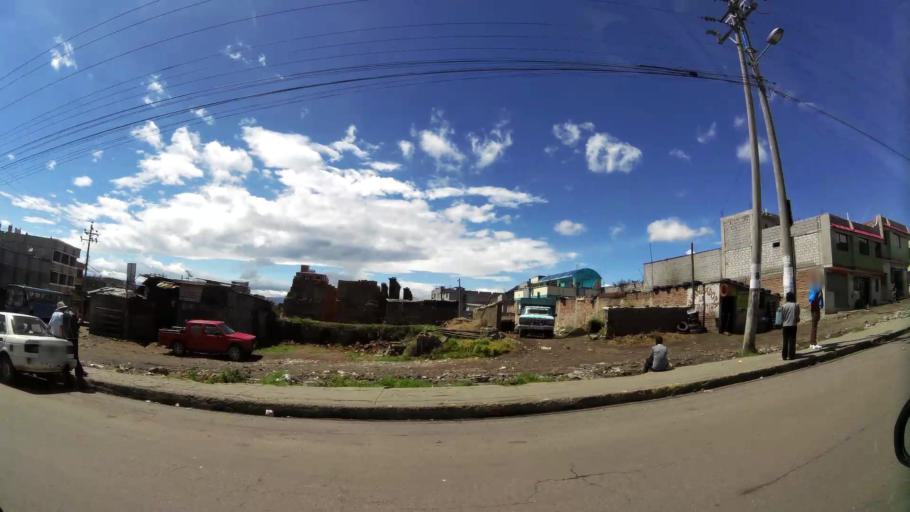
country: EC
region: Pichincha
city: Quito
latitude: -0.3213
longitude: -78.5644
